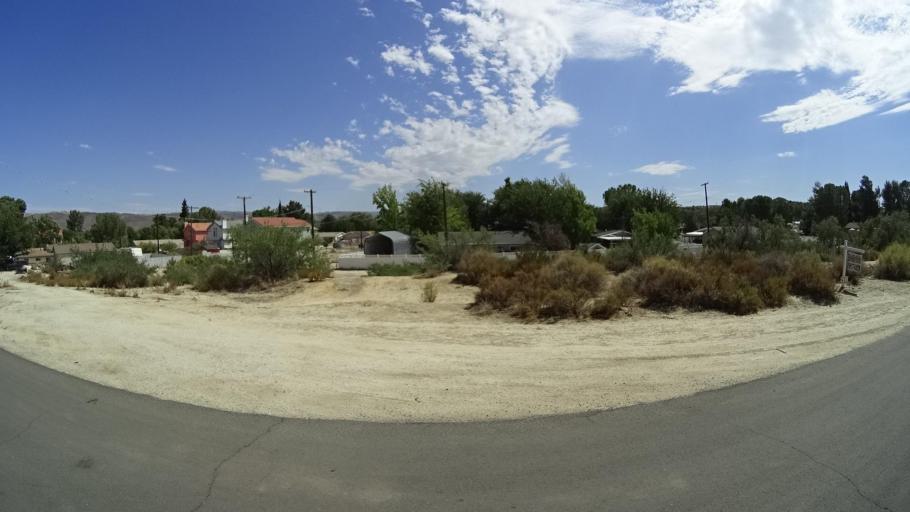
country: MX
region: Baja California
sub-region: Tecate
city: Cereso del Hongo
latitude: 32.6208
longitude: -116.1902
